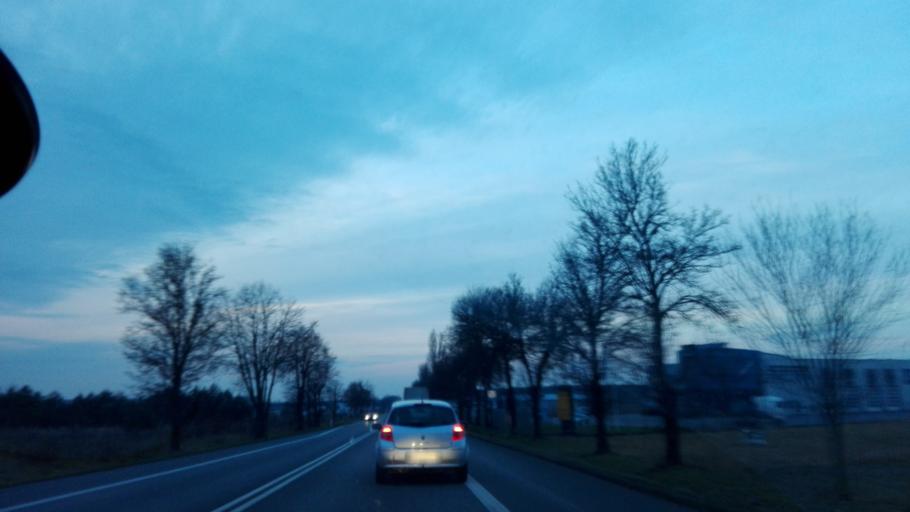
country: PL
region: Masovian Voivodeship
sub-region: Powiat siedlecki
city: Skorzec
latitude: 52.1789
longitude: 22.1728
